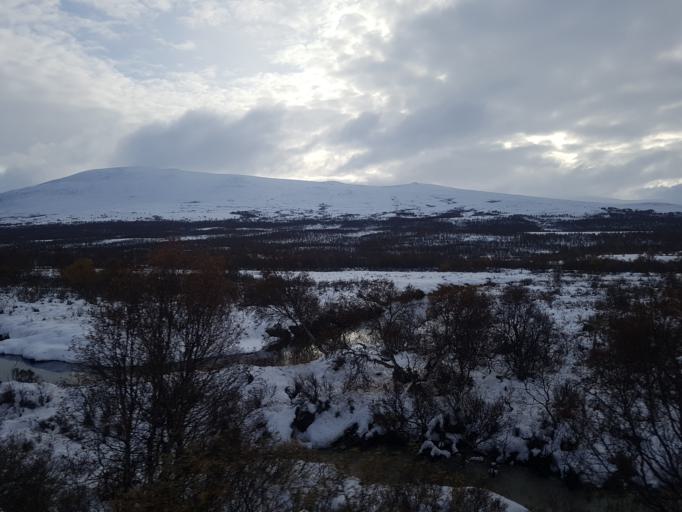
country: NO
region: Oppland
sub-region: Dovre
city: Dovre
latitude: 62.1289
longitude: 9.3032
